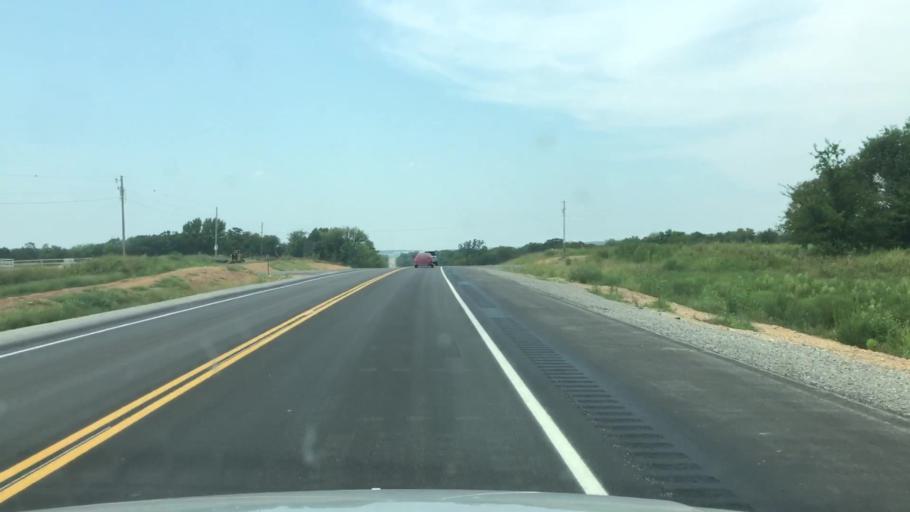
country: US
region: Oklahoma
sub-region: Muskogee County
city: Fort Gibson
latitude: 35.9369
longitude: -95.1708
